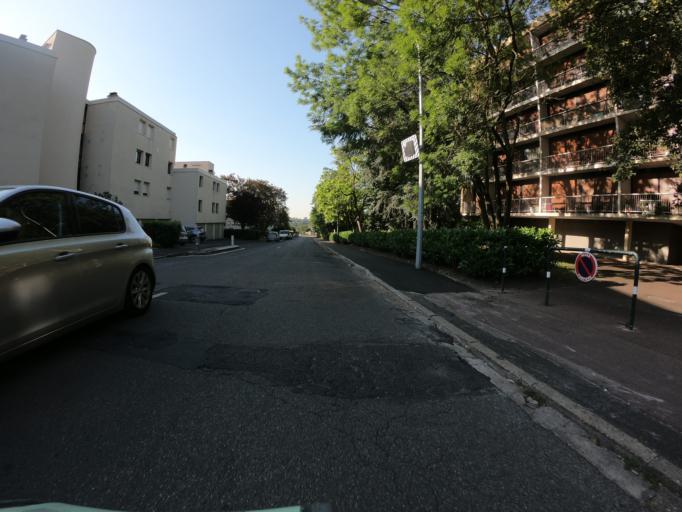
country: FR
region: Ile-de-France
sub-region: Departement de l'Essonne
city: Verrieres-le-Buisson
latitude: 48.7482
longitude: 2.2742
